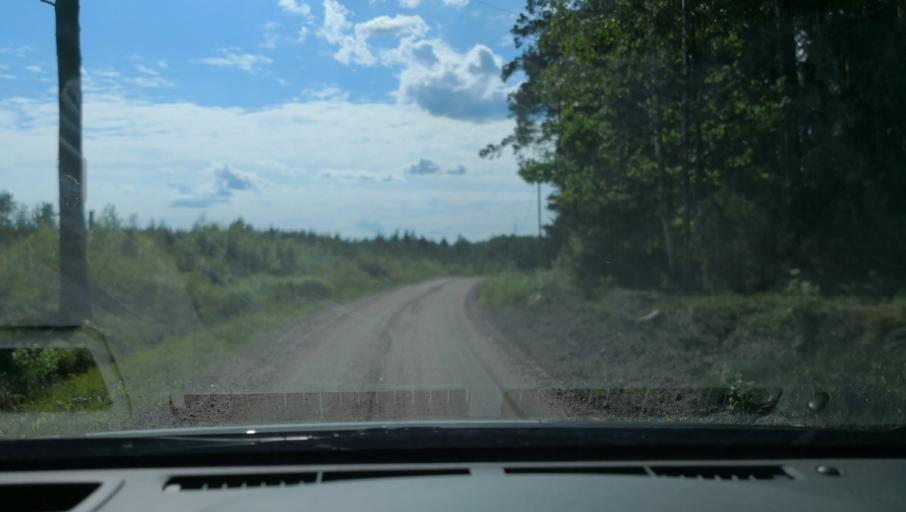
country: SE
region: Uppsala
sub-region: Enkopings Kommun
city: Orsundsbro
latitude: 59.8338
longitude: 17.2420
